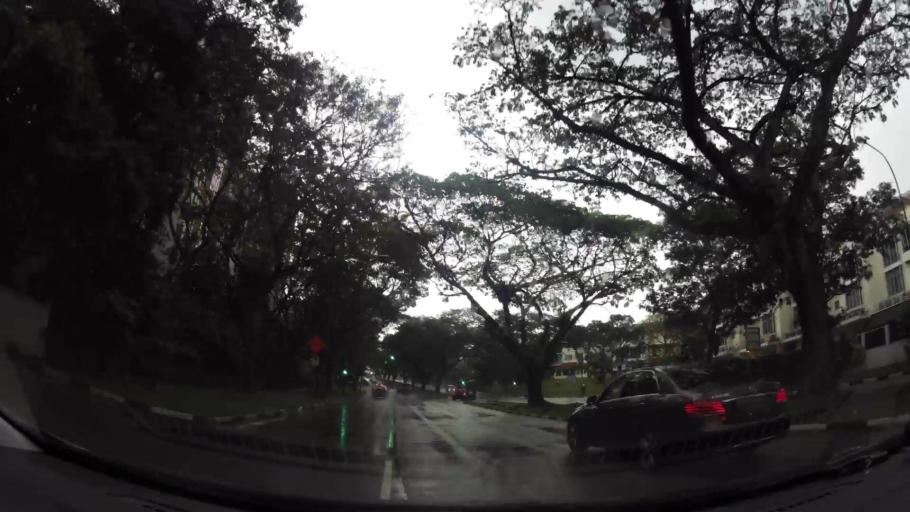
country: MY
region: Johor
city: Kampung Pasir Gudang Baru
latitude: 1.3864
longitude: 103.8398
